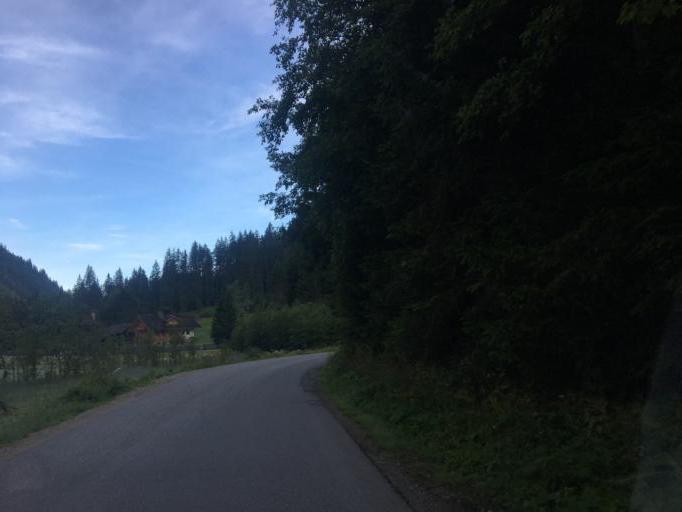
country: AT
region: Styria
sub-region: Politischer Bezirk Liezen
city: Schladming
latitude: 47.3408
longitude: 13.7387
